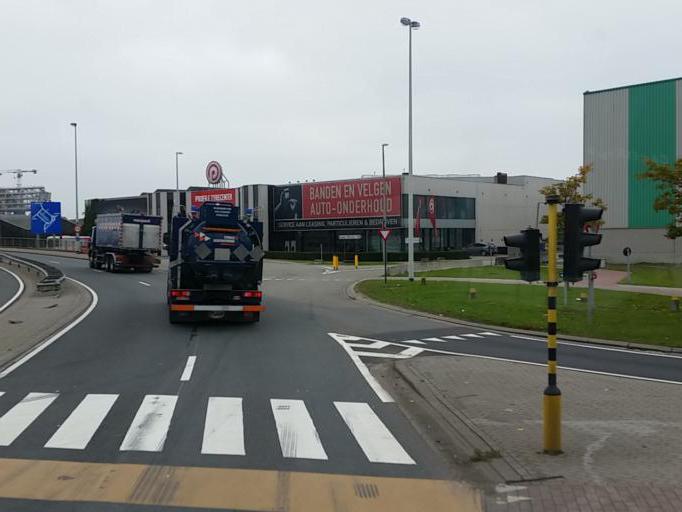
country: BE
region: Flanders
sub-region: Provincie Antwerpen
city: Antwerpen
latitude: 51.2450
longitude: 4.4139
